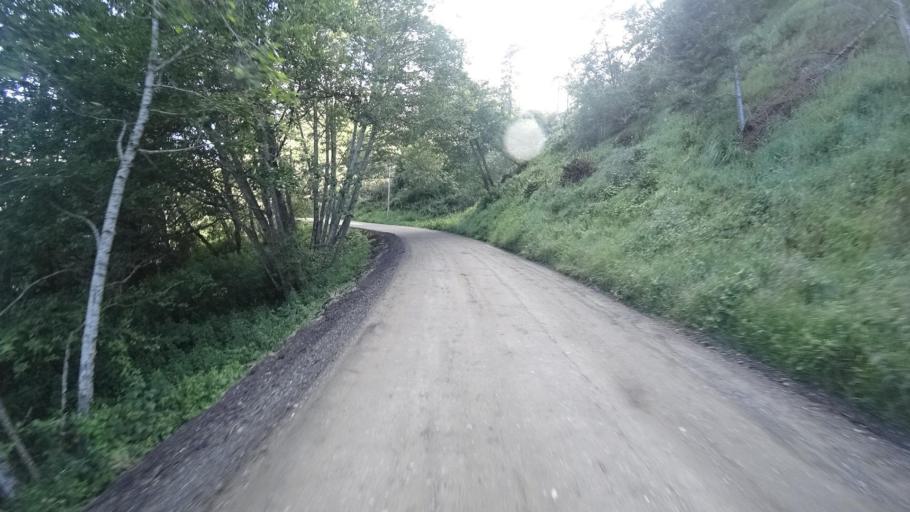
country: US
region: California
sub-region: Humboldt County
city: Westhaven-Moonstone
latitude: 41.0504
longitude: -124.1262
